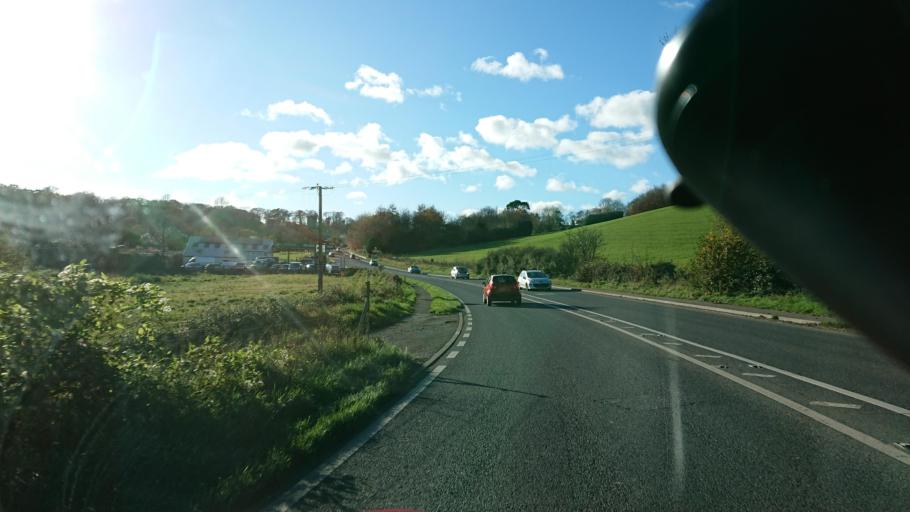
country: GB
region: England
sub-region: Cornwall
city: Pillaton
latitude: 50.4162
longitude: -4.3211
